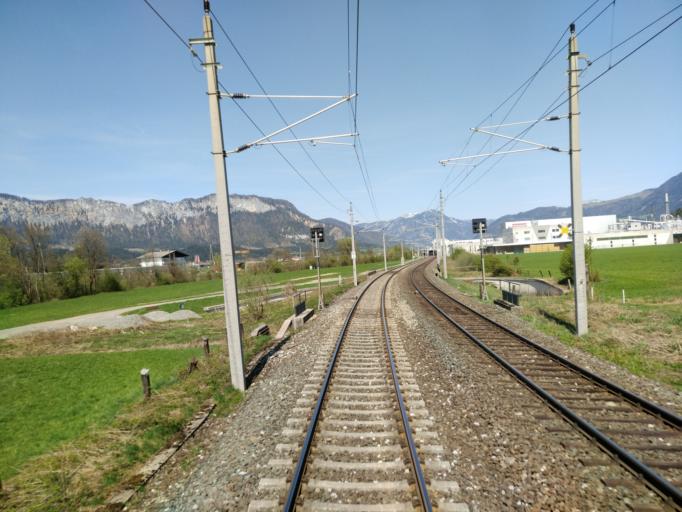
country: AT
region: Tyrol
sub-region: Politischer Bezirk Kitzbuhel
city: Oberndorf in Tirol
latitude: 47.5023
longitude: 12.3940
